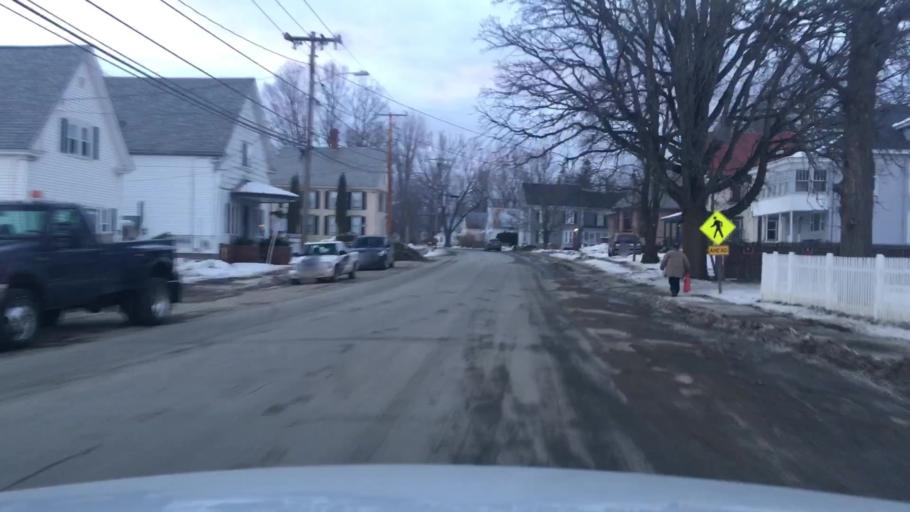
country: US
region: Maine
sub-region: Kennebec County
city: Clinton
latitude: 44.6379
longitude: -69.5030
